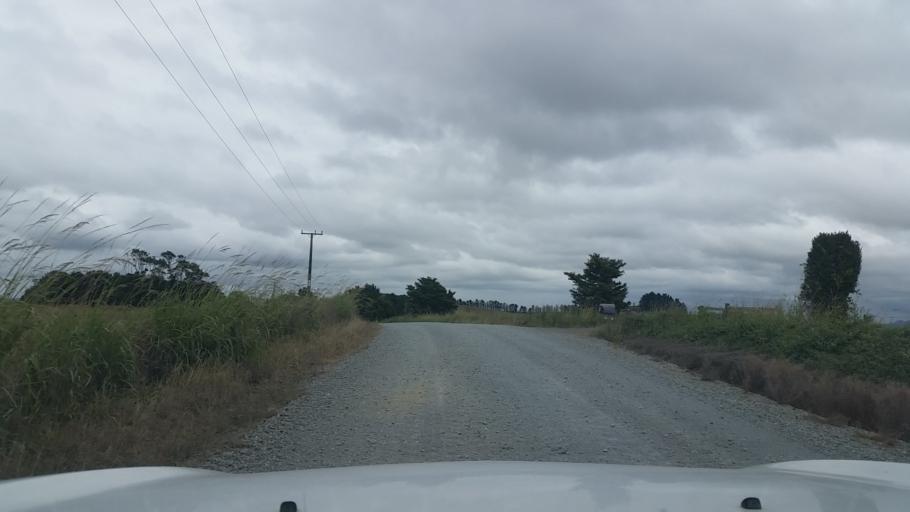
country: NZ
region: Northland
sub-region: Whangarei
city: Maungatapere
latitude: -35.6783
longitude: 174.1483
